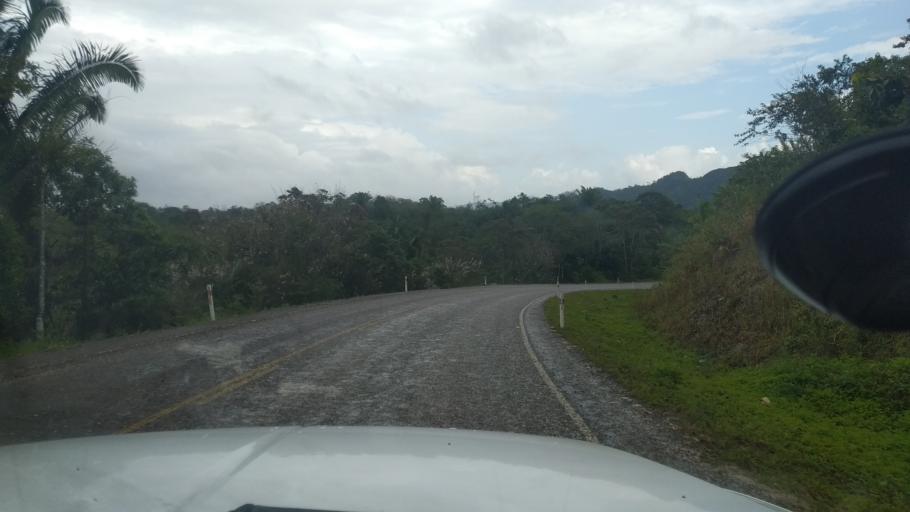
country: GT
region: Peten
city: San Luis
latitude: 16.1847
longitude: -89.2063
